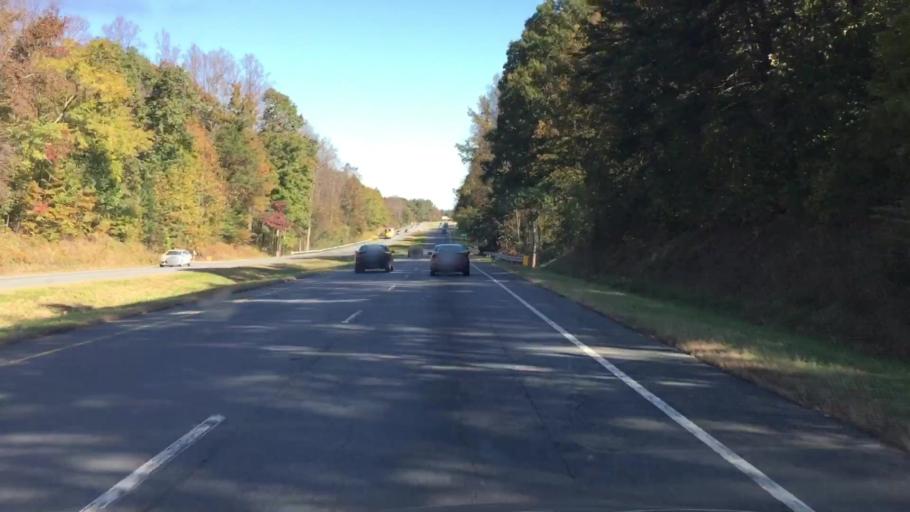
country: US
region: North Carolina
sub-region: Rockingham County
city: Reidsville
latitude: 36.2348
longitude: -79.6737
